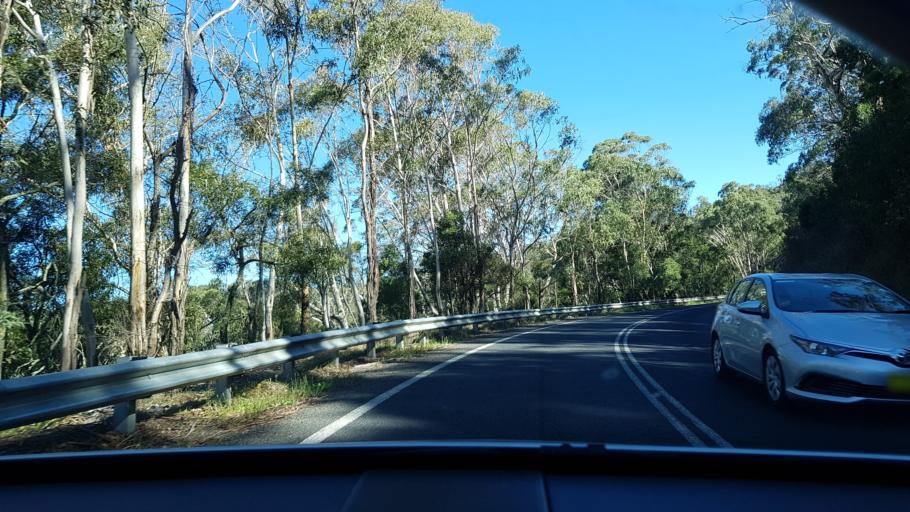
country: AU
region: New South Wales
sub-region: Lithgow
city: Bowenfels
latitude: -33.6636
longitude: 150.0509
